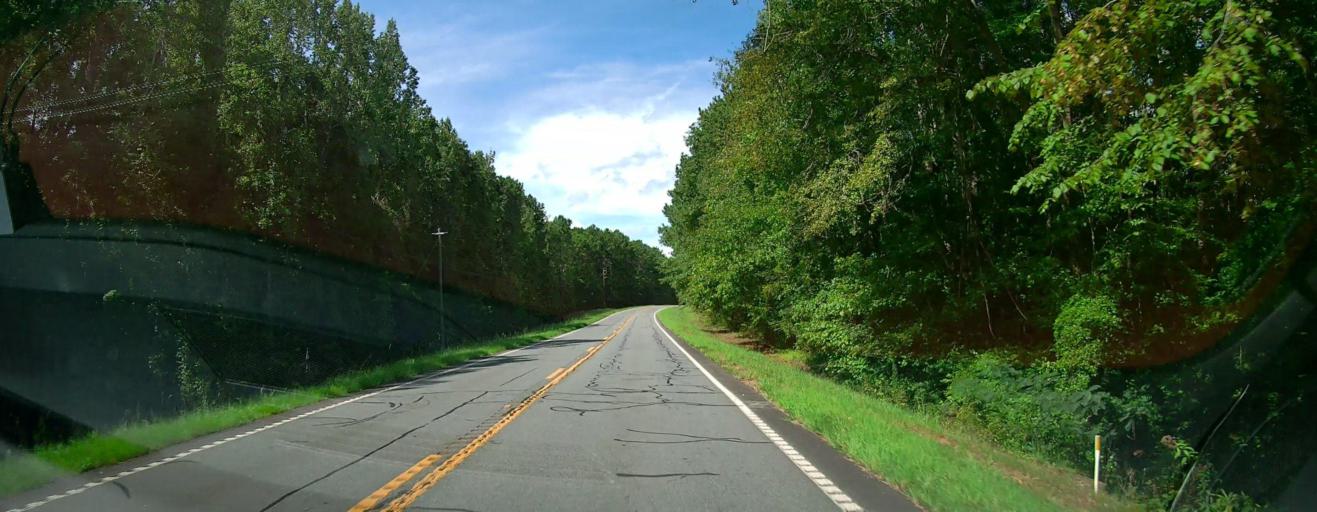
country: US
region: Georgia
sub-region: Talbot County
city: Talbotton
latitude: 32.7141
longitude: -84.5567
